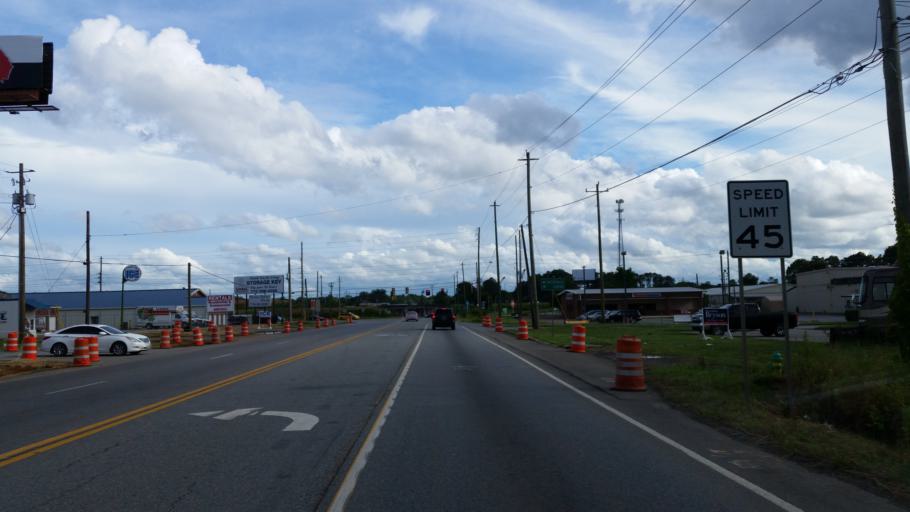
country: US
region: Georgia
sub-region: Bartow County
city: Cartersville
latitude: 34.2043
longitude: -84.7996
